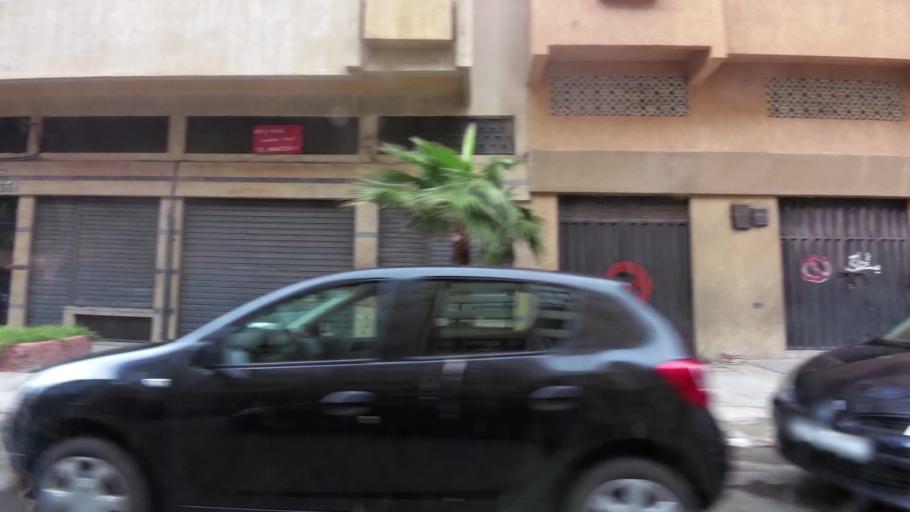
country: MA
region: Grand Casablanca
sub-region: Casablanca
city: Casablanca
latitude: 33.6000
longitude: -7.6458
